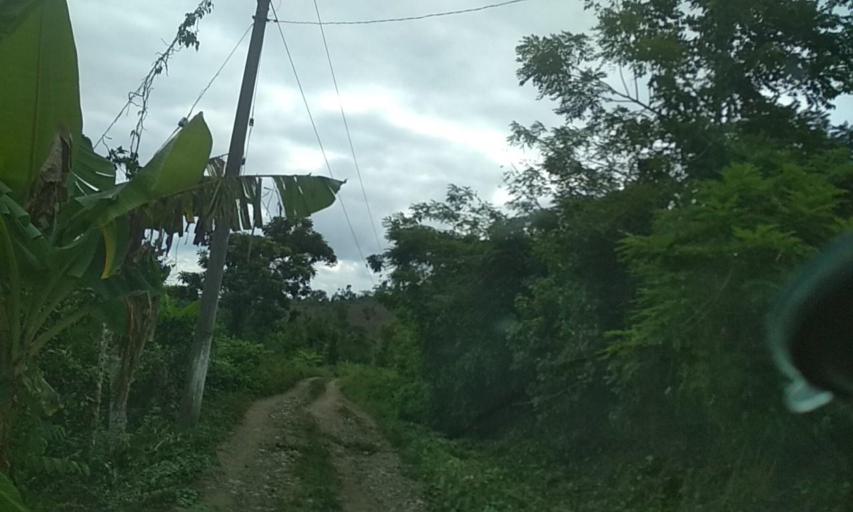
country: MX
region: Veracruz
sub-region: Papantla
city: Polutla
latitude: 20.5894
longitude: -97.2783
